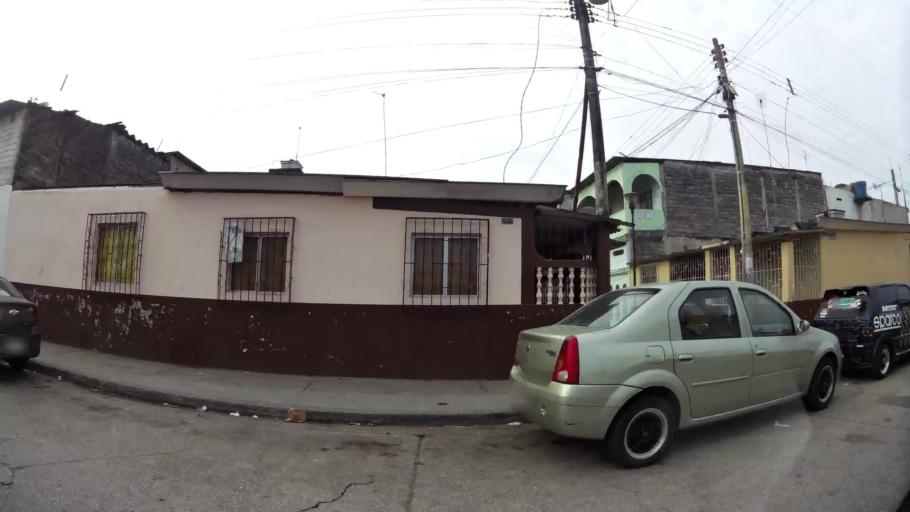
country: EC
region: Guayas
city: Guayaquil
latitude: -2.2529
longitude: -79.8868
